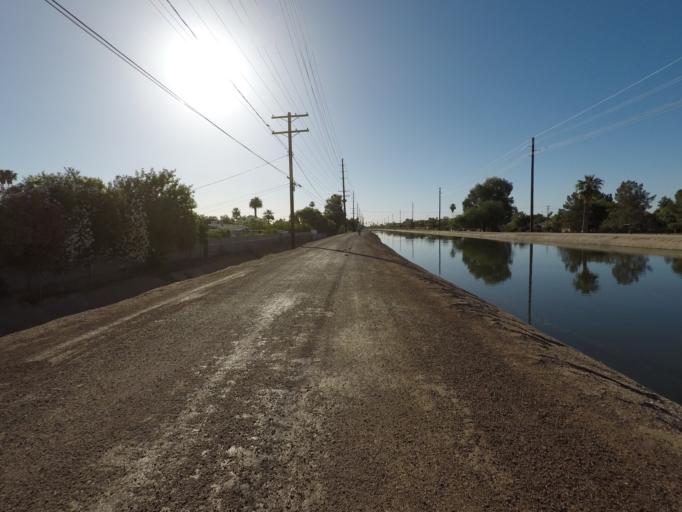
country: US
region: Arizona
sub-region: Maricopa County
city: Paradise Valley
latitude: 33.4920
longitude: -111.9563
